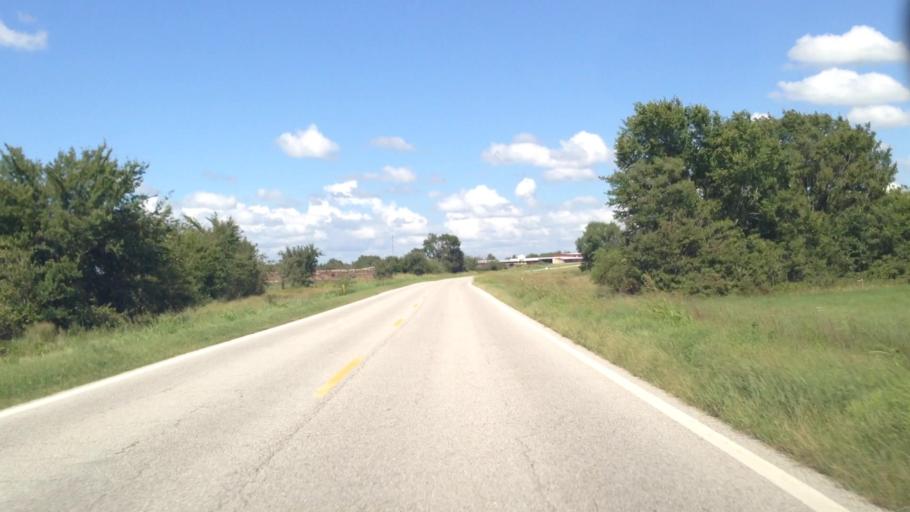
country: US
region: Kansas
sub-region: Labette County
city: Chetopa
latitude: 36.8588
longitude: -95.1169
